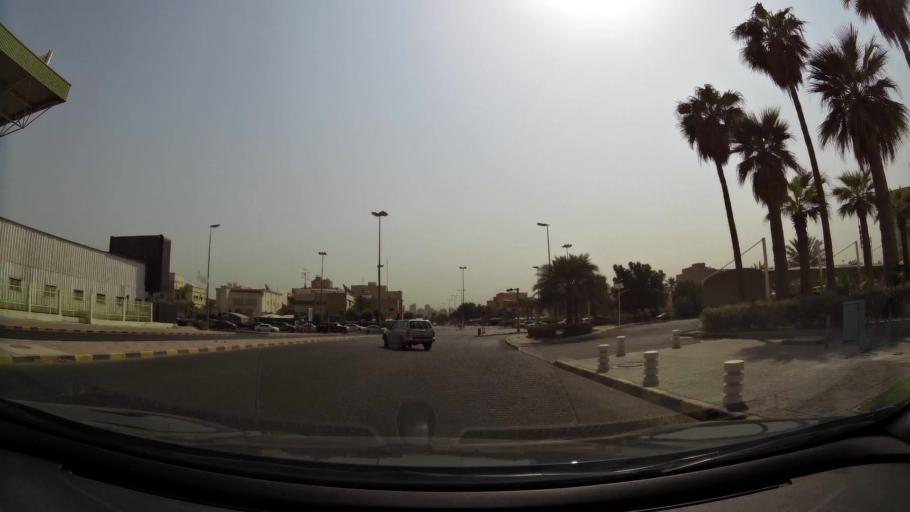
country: KW
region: Al Asimah
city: Ad Dasmah
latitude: 29.3552
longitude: 47.9999
